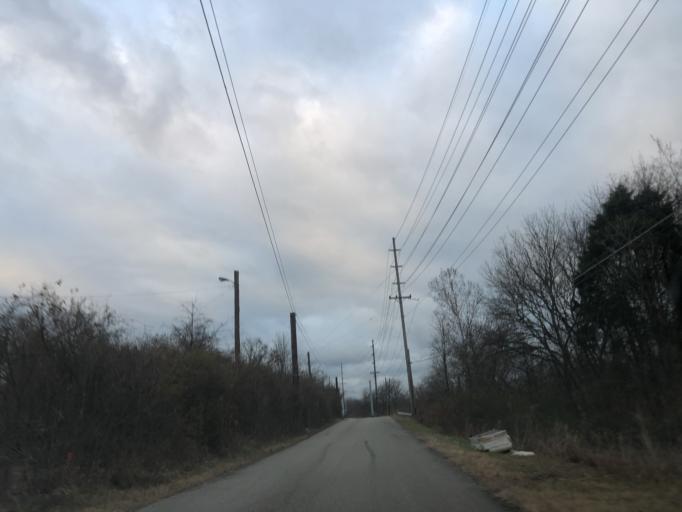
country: US
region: Tennessee
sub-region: Davidson County
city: Goodlettsville
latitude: 36.2873
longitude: -86.7000
